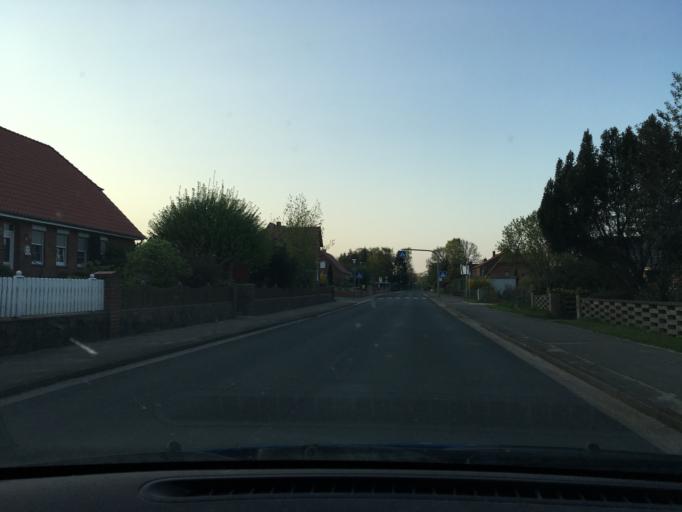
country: DE
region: Lower Saxony
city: Sudergellersen
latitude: 53.2122
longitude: 10.2977
